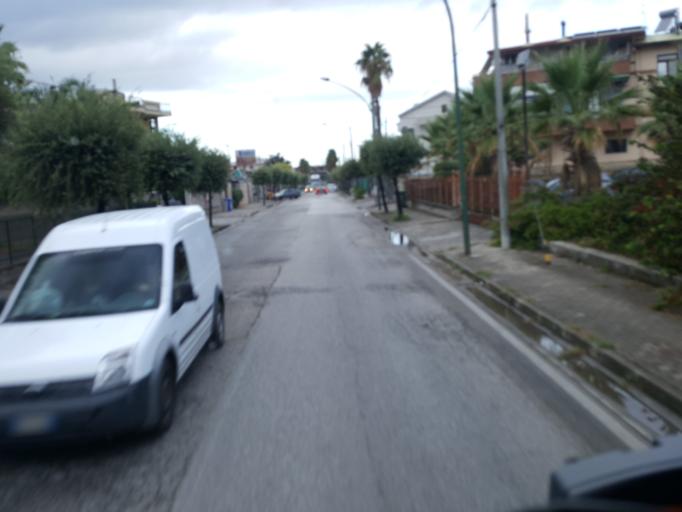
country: IT
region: Campania
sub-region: Provincia di Napoli
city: Palma Campania
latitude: 40.8580
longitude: 14.5517
